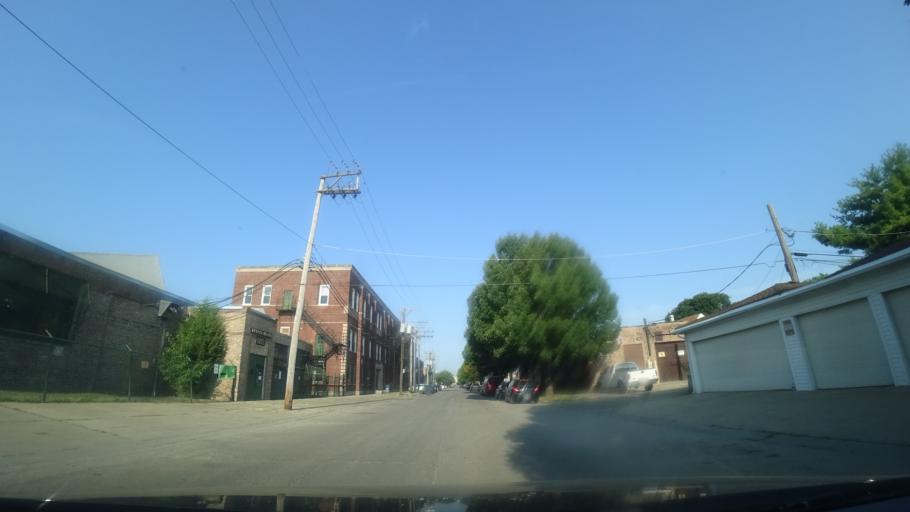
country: US
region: Illinois
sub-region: Cook County
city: Oak Park
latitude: 41.9180
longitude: -87.7710
